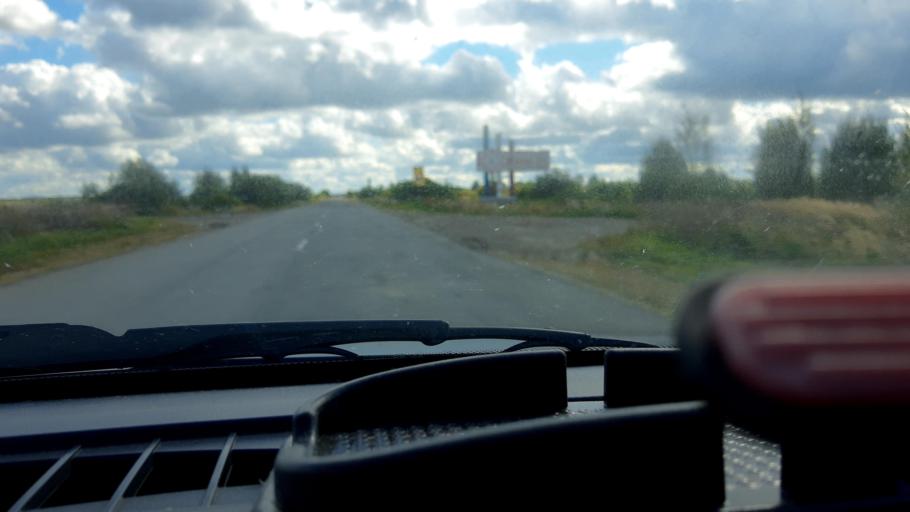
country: RU
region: Nizjnij Novgorod
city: Sharanga
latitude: 56.9423
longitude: 46.6437
